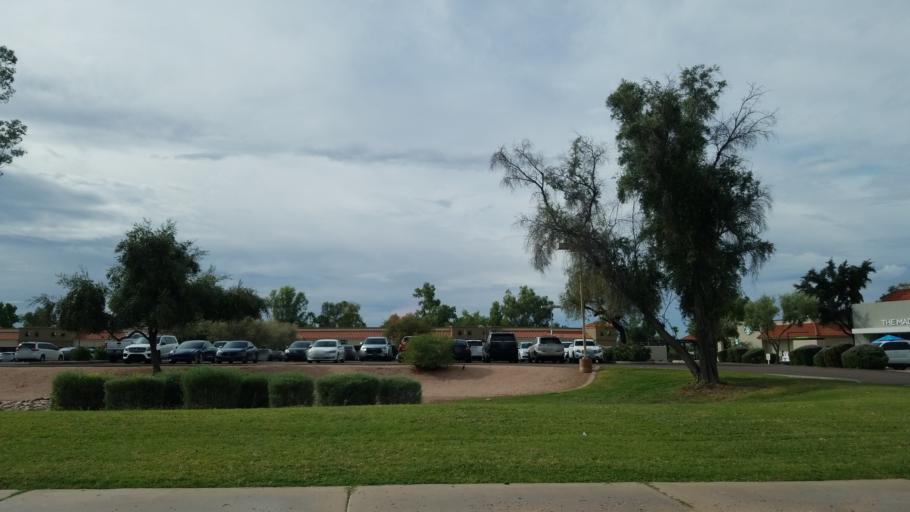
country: US
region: Arizona
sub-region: Maricopa County
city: Paradise Valley
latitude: 33.5754
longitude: -111.9049
